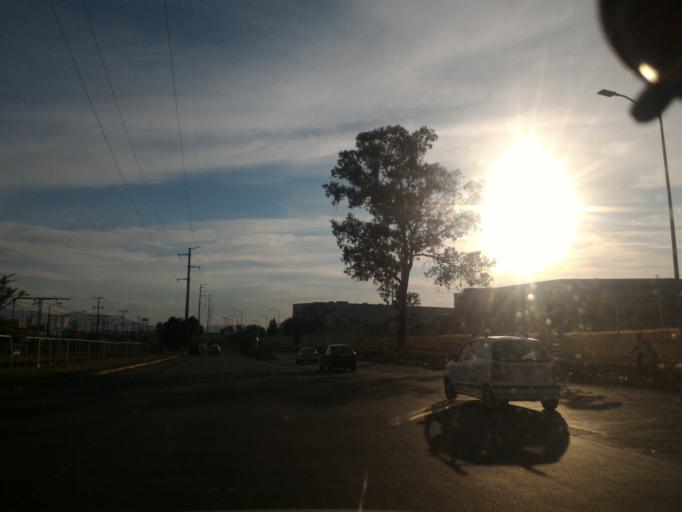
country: MX
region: Jalisco
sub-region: San Pedro Tlaquepaque
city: Paseo del Prado
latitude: 20.6101
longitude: -103.3989
